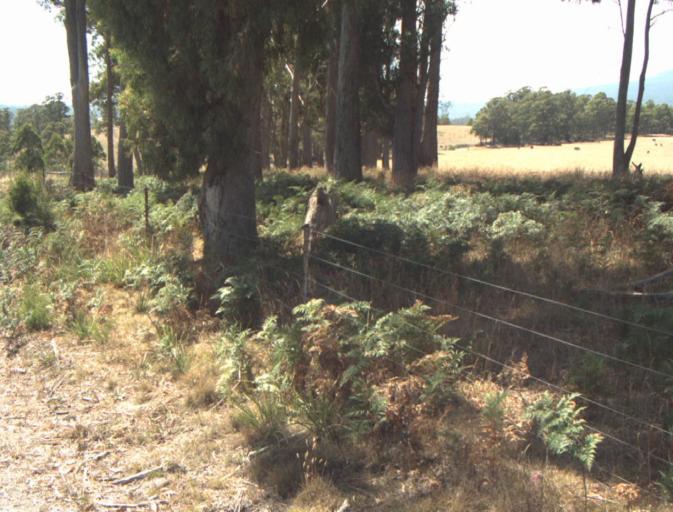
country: AU
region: Tasmania
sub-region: Launceston
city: Mayfield
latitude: -41.2480
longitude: 147.1662
